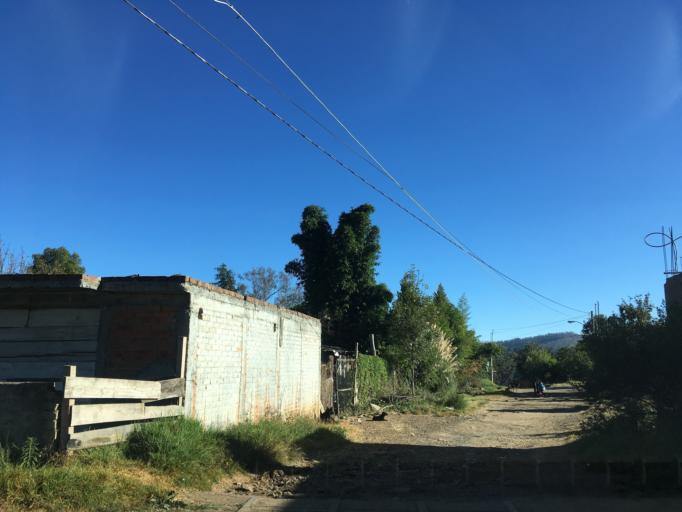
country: MX
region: Michoacan
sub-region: Morelia
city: Montana Monarca (Punta Altozano)
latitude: 19.6539
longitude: -101.1502
